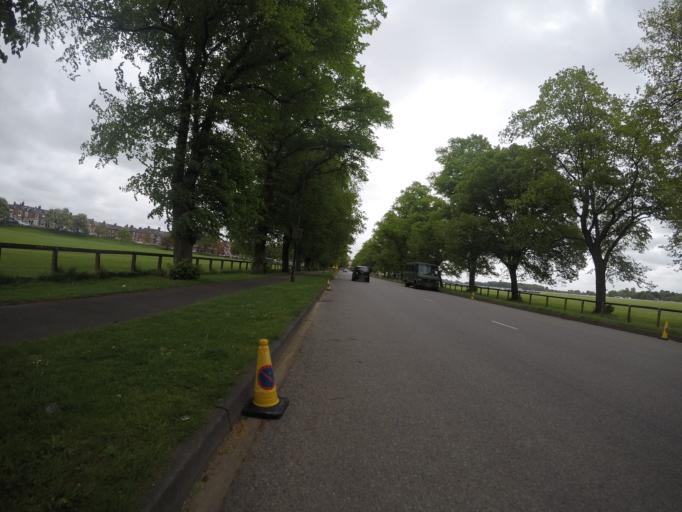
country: GB
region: England
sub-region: City of York
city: York
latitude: 53.9459
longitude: -1.0962
